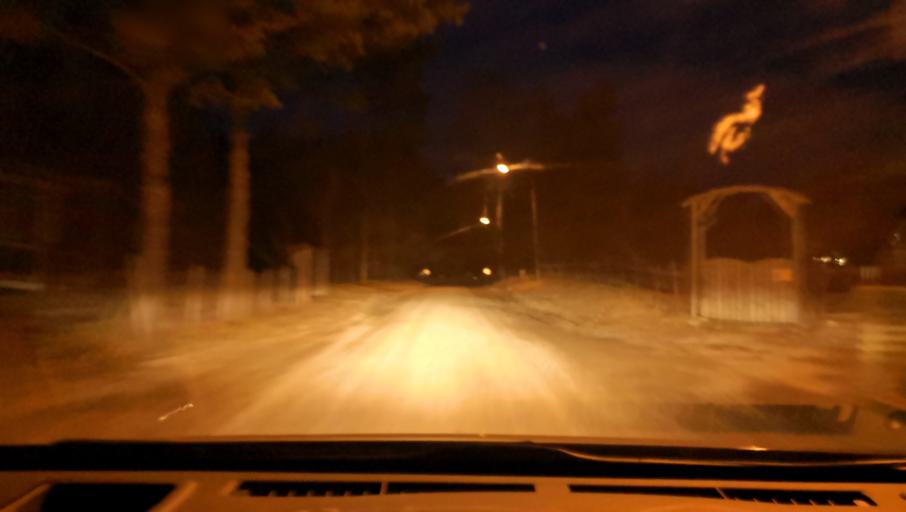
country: SE
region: Vaestmanland
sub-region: Skinnskattebergs Kommun
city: Skinnskatteberg
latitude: 59.6625
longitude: 15.5344
